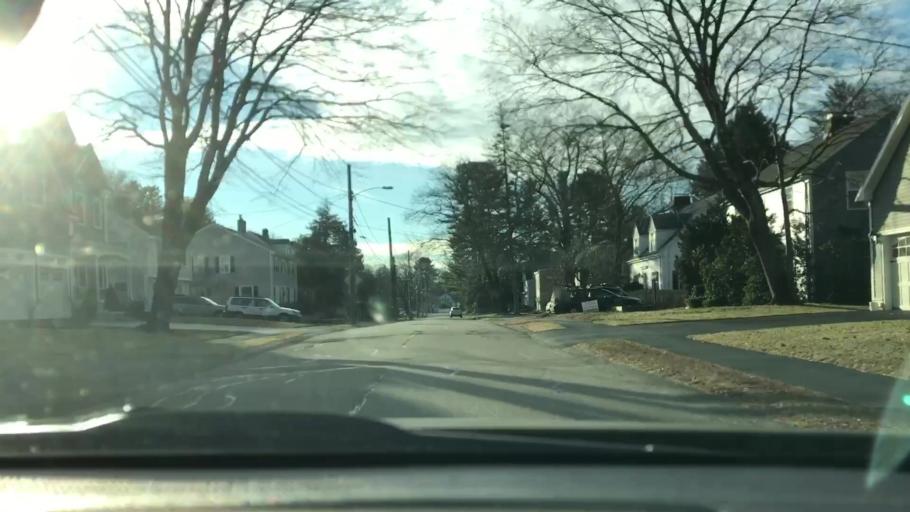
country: US
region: Massachusetts
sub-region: Norfolk County
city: Needham
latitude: 42.2909
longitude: -71.2290
